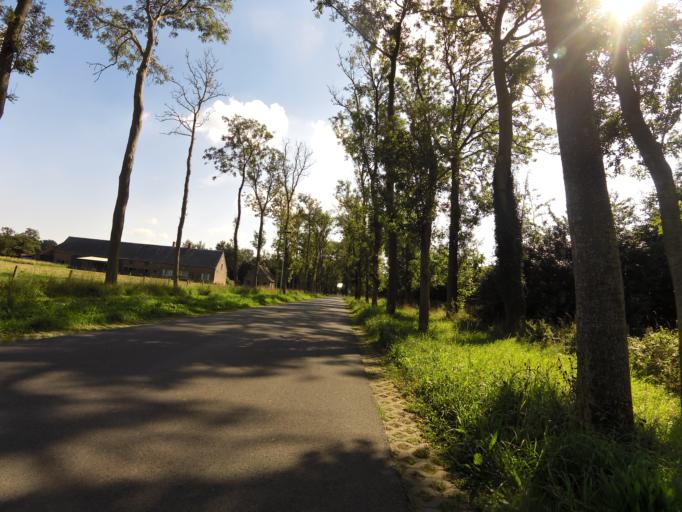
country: BE
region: Flanders
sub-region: Provincie West-Vlaanderen
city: Zedelgem
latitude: 51.1977
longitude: 3.1515
